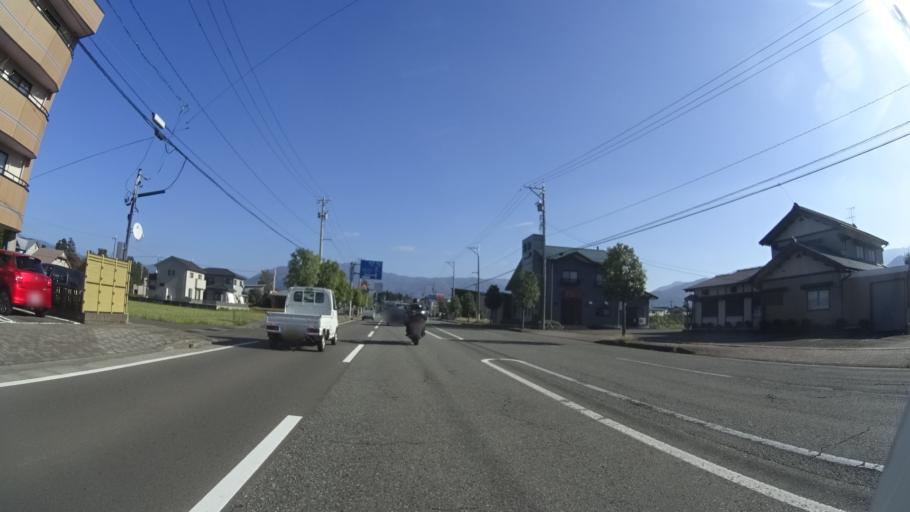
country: JP
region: Fukui
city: Ono
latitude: 35.9709
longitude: 136.4856
